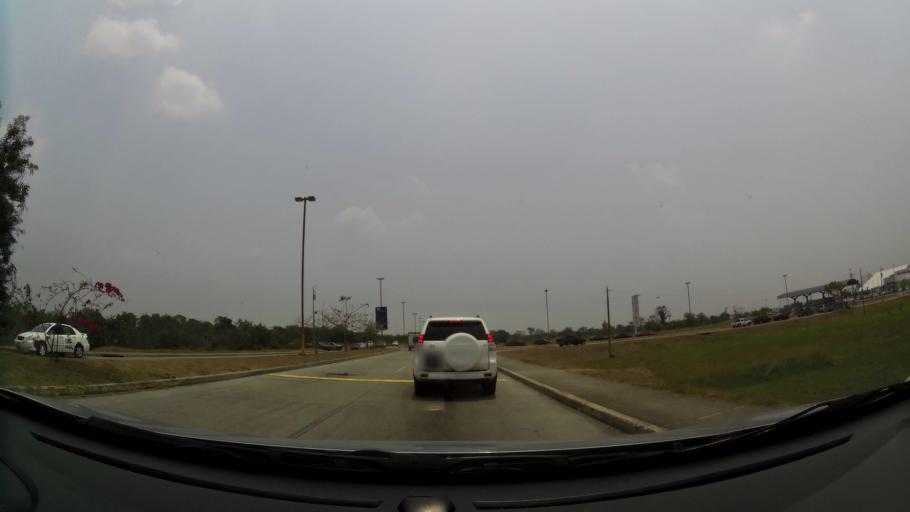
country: HN
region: Cortes
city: La Lima
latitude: 15.4567
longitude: -87.9305
